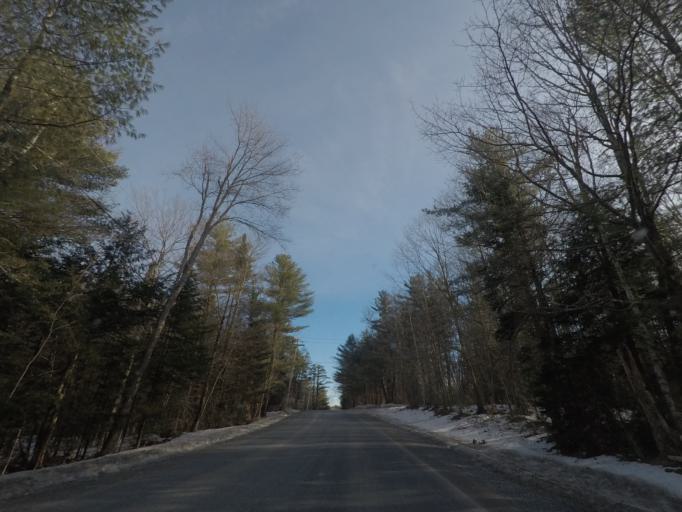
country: US
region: New York
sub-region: Rensselaer County
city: Hoosick Falls
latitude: 42.7668
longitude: -73.4279
